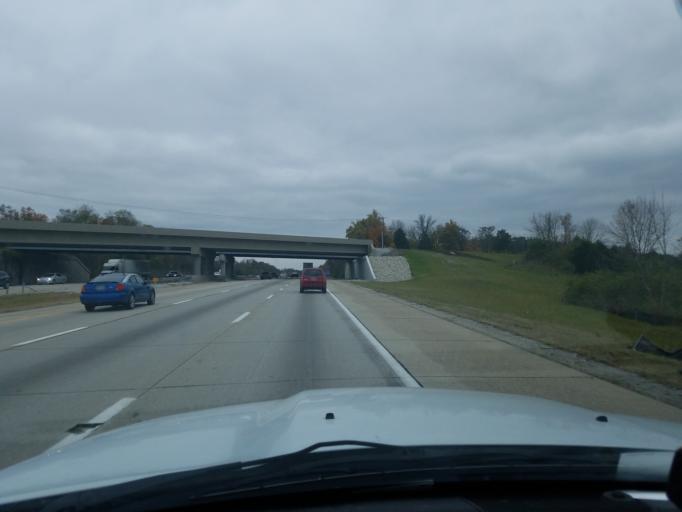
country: US
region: Kentucky
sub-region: Bullitt County
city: Shepherdsville
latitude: 38.0232
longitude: -85.6968
